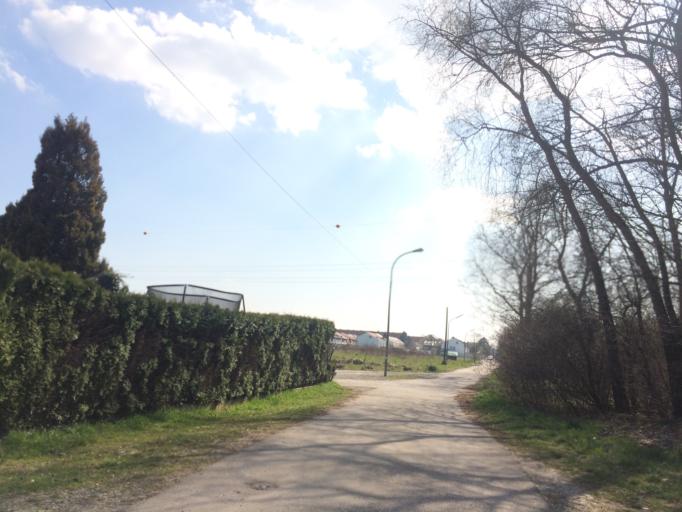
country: DE
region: Bavaria
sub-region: Swabia
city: Gersthofen
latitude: 48.4123
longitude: 10.8974
